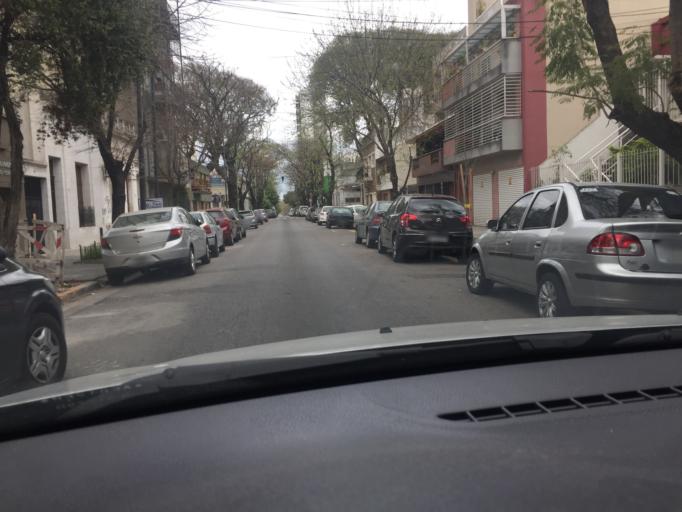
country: AR
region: Buenos Aires
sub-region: Partido de General San Martin
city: General San Martin
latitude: -34.5684
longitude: -58.4902
